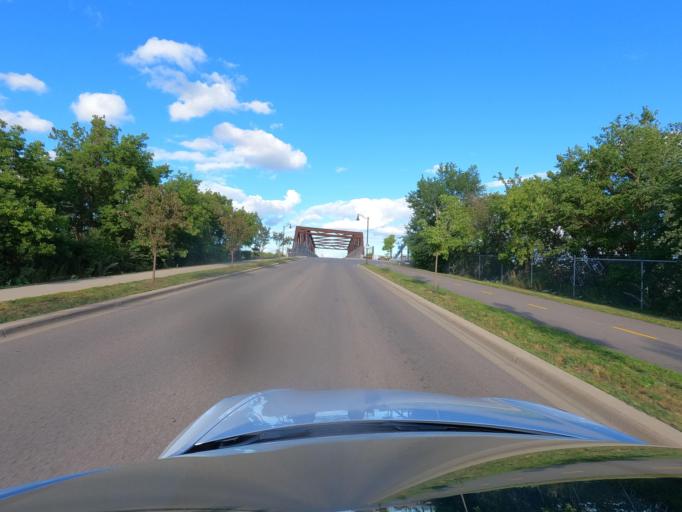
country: US
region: Minnesota
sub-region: Anoka County
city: Columbia Heights
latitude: 45.0276
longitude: -93.2699
